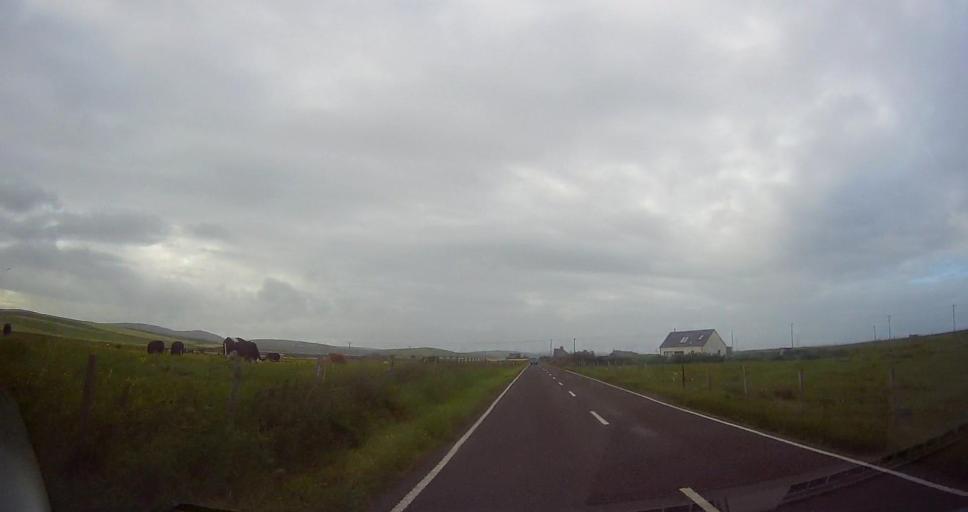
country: GB
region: Scotland
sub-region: Orkney Islands
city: Stromness
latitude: 58.9768
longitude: -3.2417
